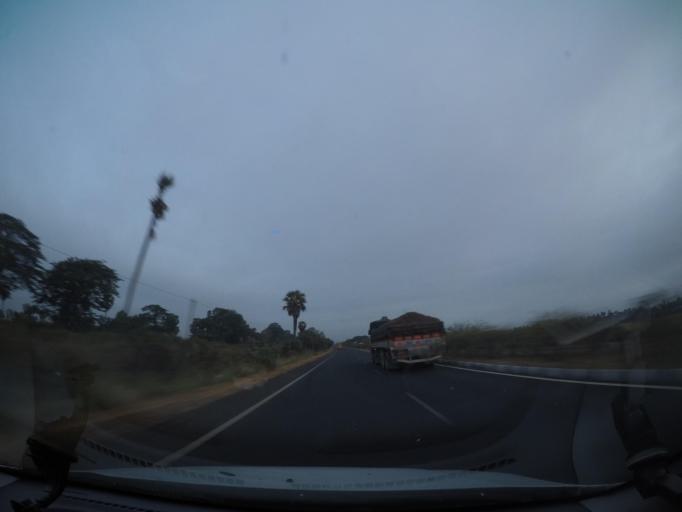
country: IN
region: Andhra Pradesh
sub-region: West Godavari
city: Tadepallegudem
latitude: 16.8101
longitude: 81.3471
